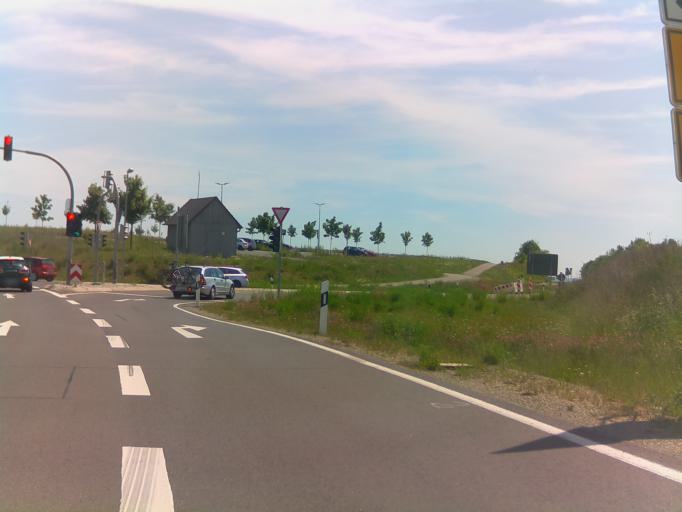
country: DE
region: Bavaria
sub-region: Regierungsbezirk Unterfranken
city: Oerlenbach
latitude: 50.1453
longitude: 10.1498
